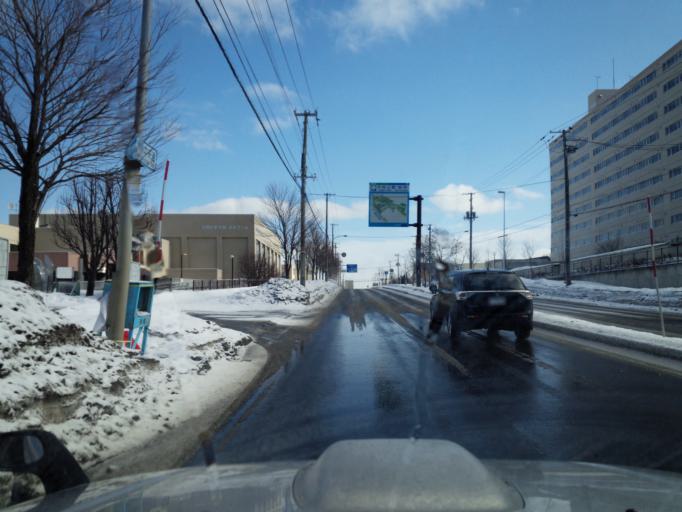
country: JP
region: Hokkaido
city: Kitahiroshima
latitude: 42.9903
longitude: 141.4515
